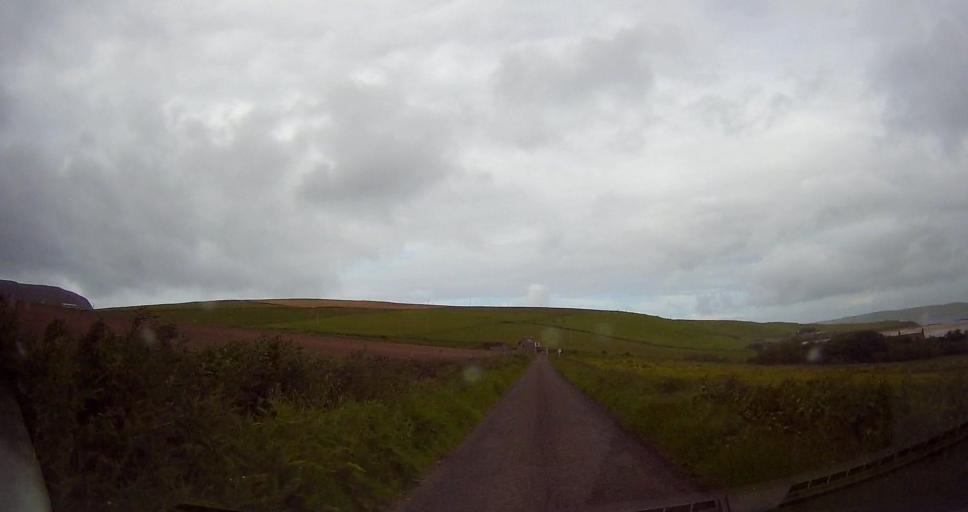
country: GB
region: Scotland
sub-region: Orkney Islands
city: Stromness
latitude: 58.9142
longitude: -3.3243
